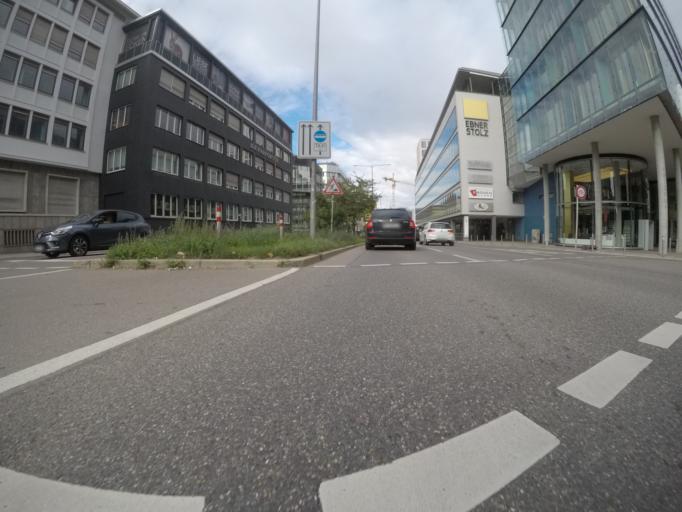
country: DE
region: Baden-Wuerttemberg
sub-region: Regierungsbezirk Stuttgart
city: Stuttgart
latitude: 48.7837
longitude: 9.1760
